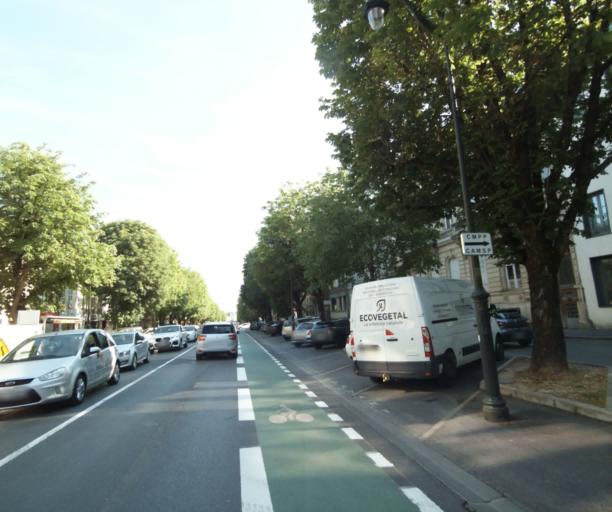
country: FR
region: Champagne-Ardenne
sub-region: Departement des Ardennes
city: Charleville-Mezieres
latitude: 49.7702
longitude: 4.7194
